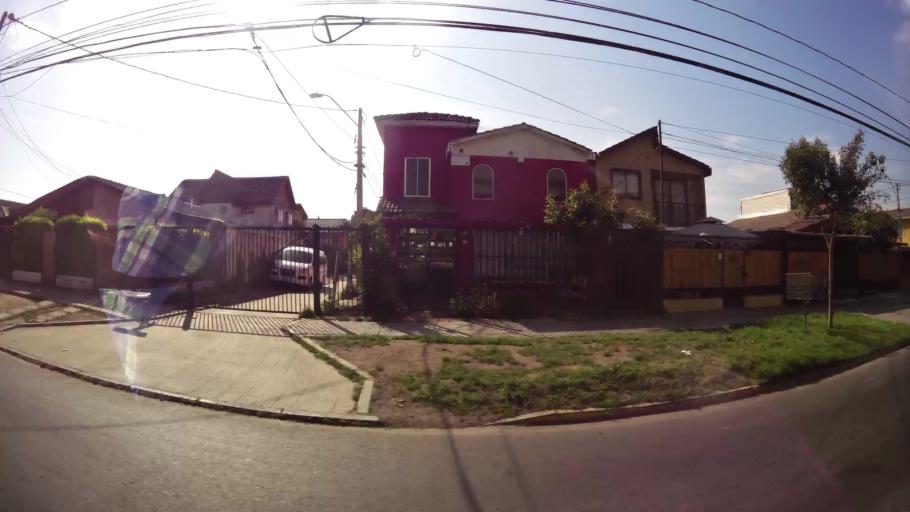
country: CL
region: Santiago Metropolitan
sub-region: Provincia de Santiago
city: Lo Prado
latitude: -33.4656
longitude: -70.7374
